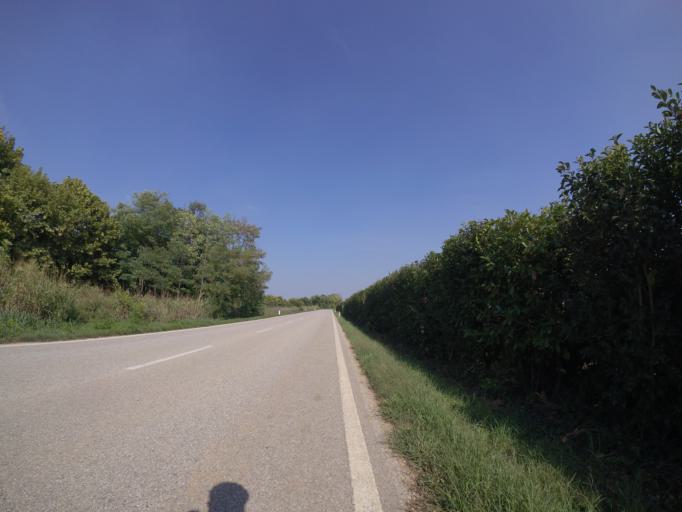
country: IT
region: Friuli Venezia Giulia
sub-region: Provincia di Udine
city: Basiliano
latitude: 46.0062
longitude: 13.0521
